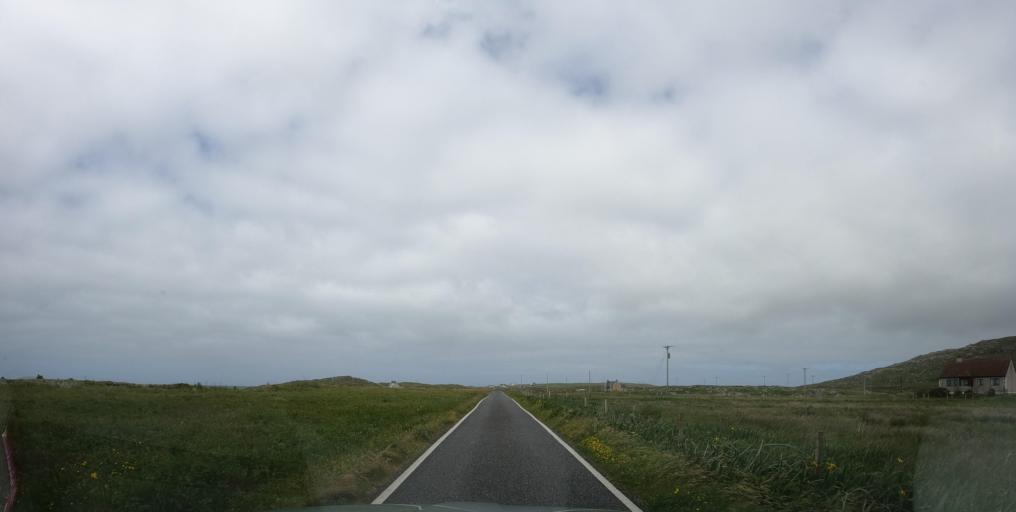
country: GB
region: Scotland
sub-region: Eilean Siar
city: Isle of South Uist
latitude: 57.1031
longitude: -7.3427
